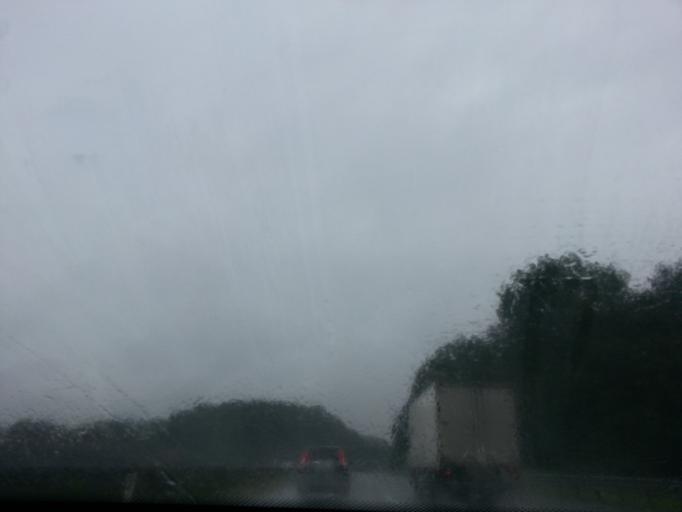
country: AT
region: Upper Austria
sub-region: Politischer Bezirk Vocklabruck
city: Desselbrunn
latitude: 47.9858
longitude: 13.7773
